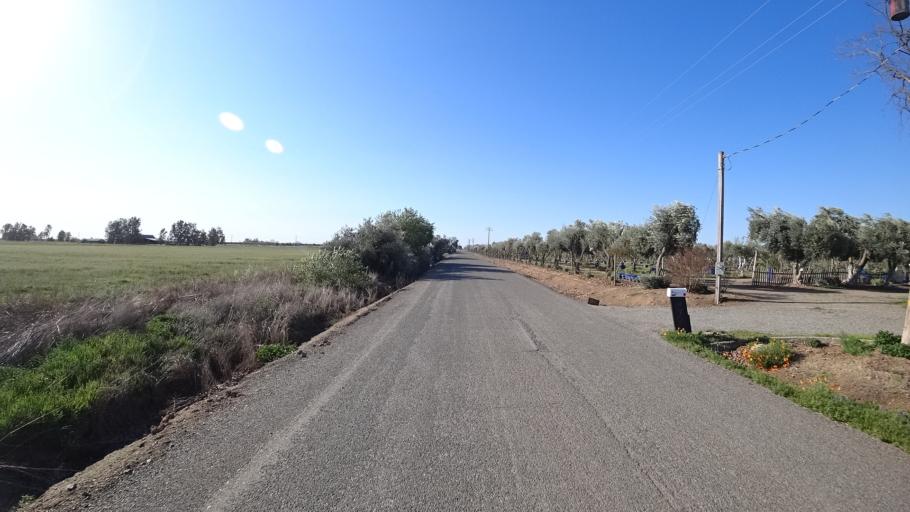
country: US
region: California
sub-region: Glenn County
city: Orland
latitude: 39.7720
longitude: -122.1227
